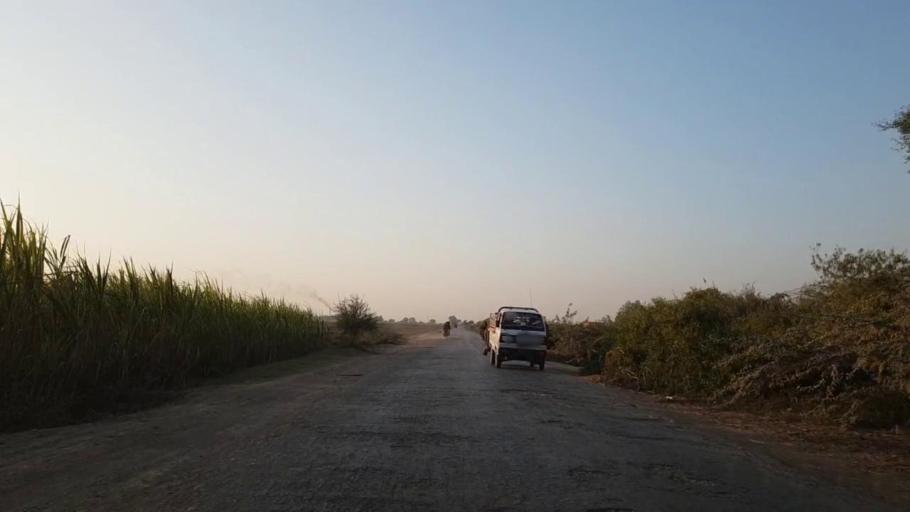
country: PK
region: Sindh
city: Chambar
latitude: 25.2428
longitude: 68.6883
